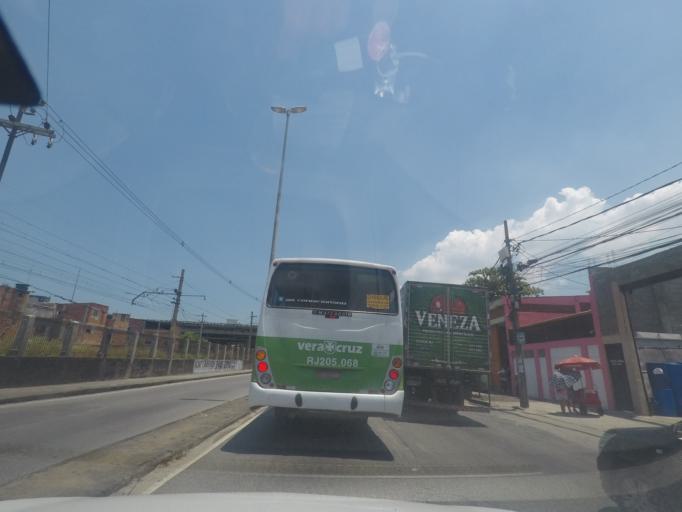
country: BR
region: Rio de Janeiro
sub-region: Duque De Caxias
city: Duque de Caxias
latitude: -22.8142
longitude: -43.3012
